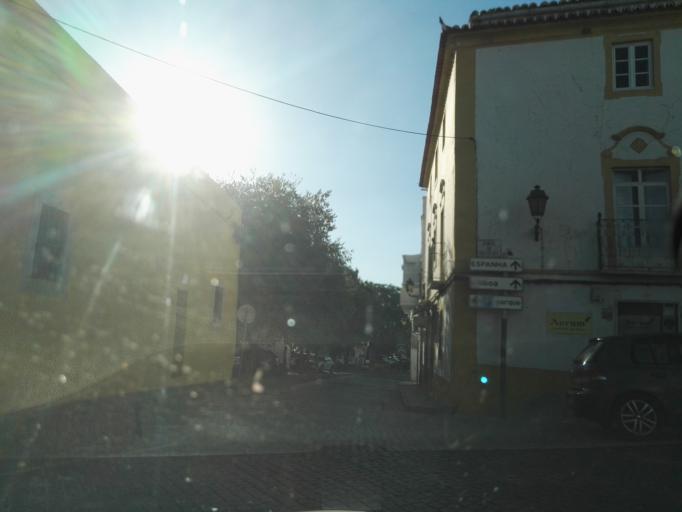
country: PT
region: Portalegre
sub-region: Elvas
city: Elvas
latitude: 38.8776
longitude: -7.1625
